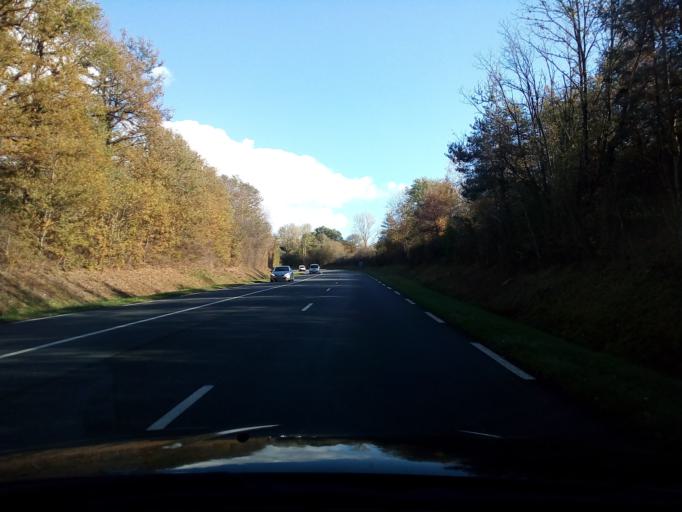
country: FR
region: Auvergne
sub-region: Departement de l'Allier
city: Montmarault
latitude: 46.3214
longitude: 3.0397
